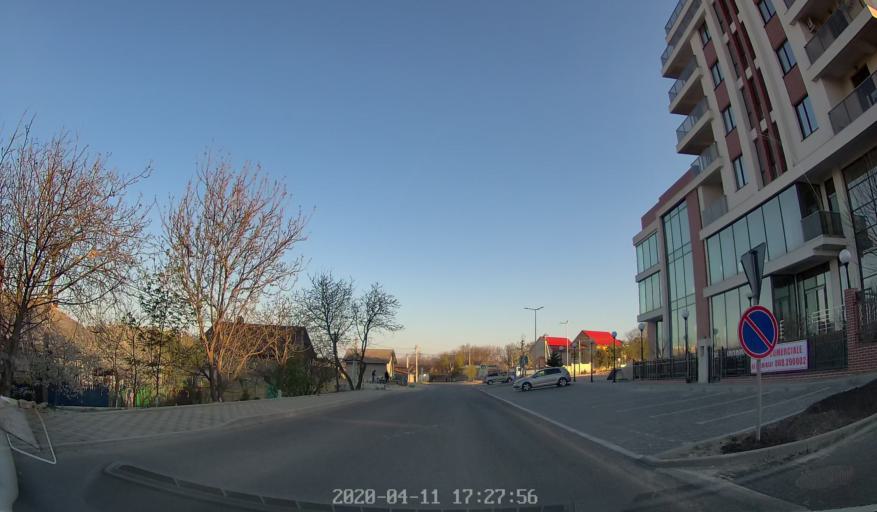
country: MD
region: Laloveni
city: Ialoveni
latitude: 47.0074
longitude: 28.7641
